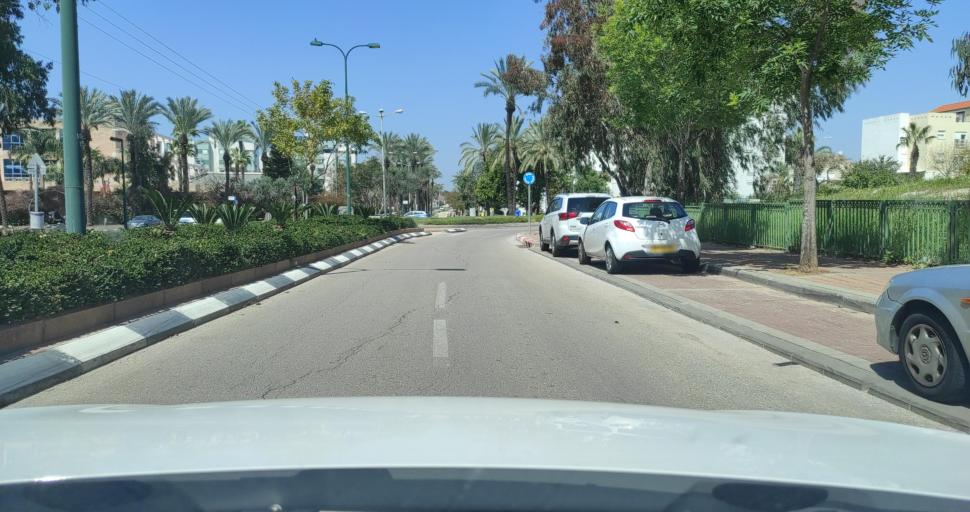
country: IL
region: Central District
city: Nordiyya
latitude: 32.3062
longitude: 34.8808
